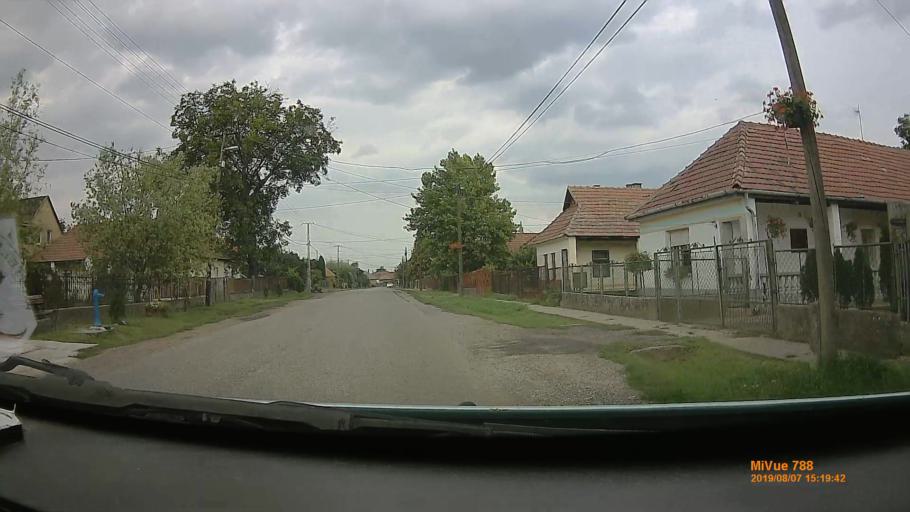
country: HU
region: Borsod-Abauj-Zemplen
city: Encs
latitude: 48.3515
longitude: 21.1439
